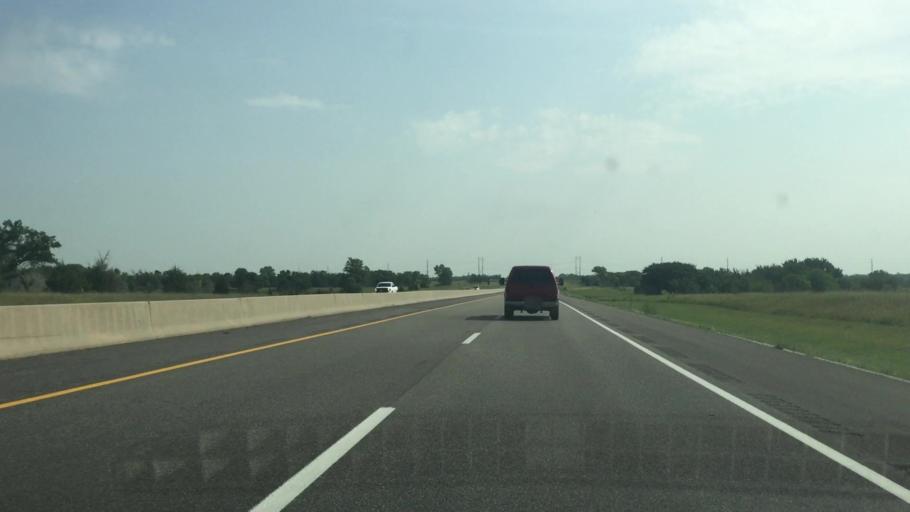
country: US
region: Kansas
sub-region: Butler County
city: Towanda
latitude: 37.7873
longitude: -96.9423
